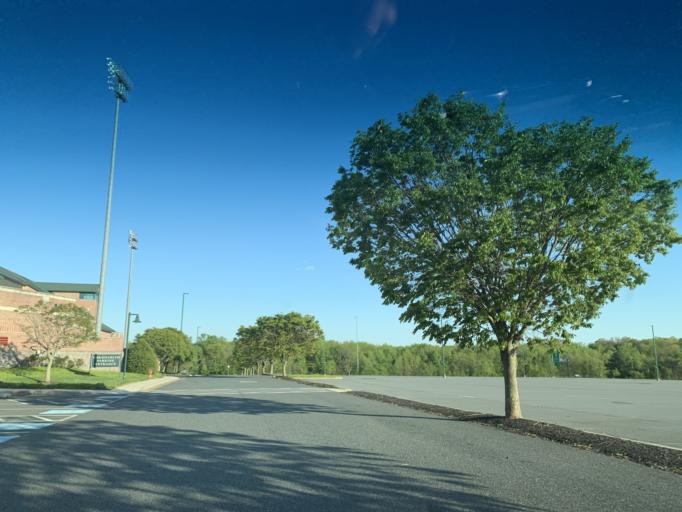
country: US
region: Maryland
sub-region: Harford County
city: Aberdeen
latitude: 39.5309
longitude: -76.1871
